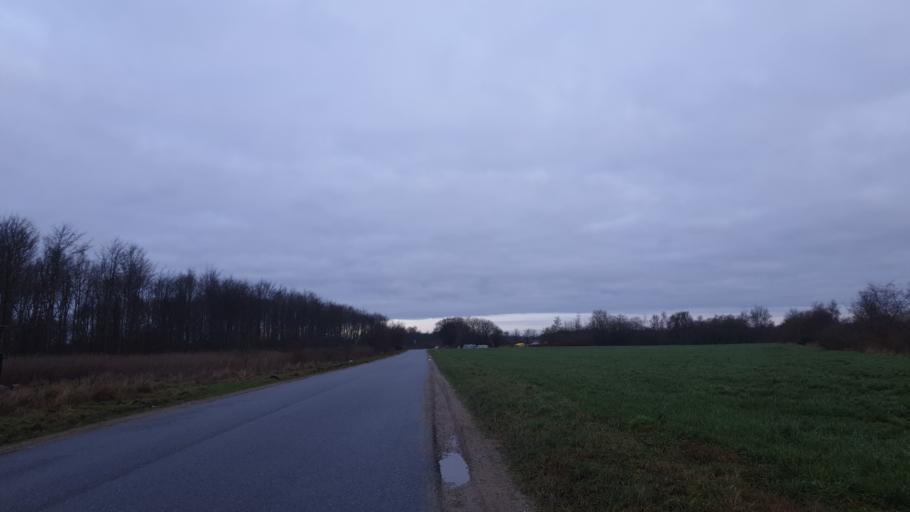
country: DK
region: Central Jutland
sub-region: Hedensted Kommune
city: Hedensted
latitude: 55.7822
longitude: 9.7004
